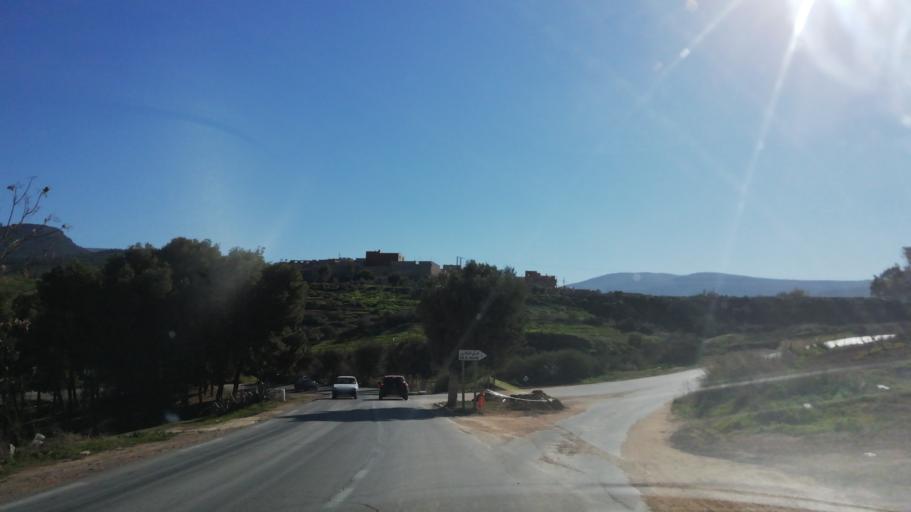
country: DZ
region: Tlemcen
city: Beni Mester
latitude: 34.8295
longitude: -1.5098
